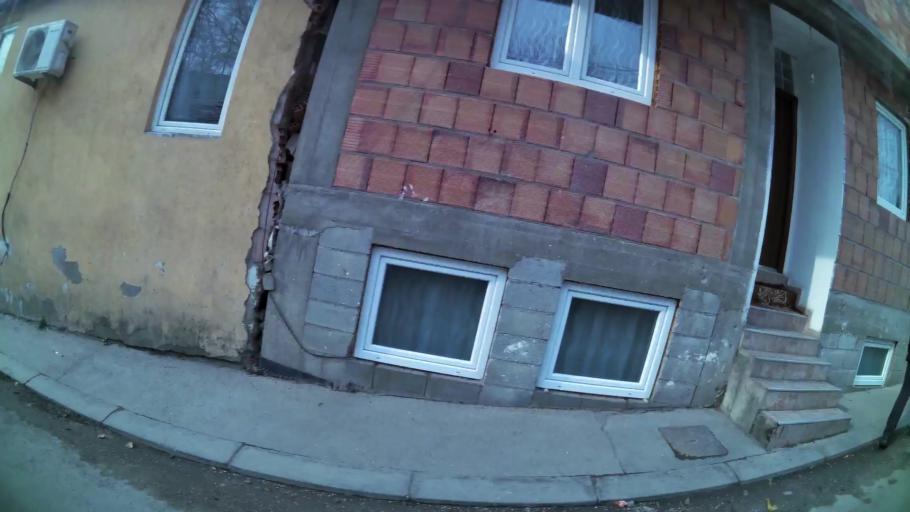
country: MK
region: Cair
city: Cair
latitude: 42.0078
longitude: 21.4466
